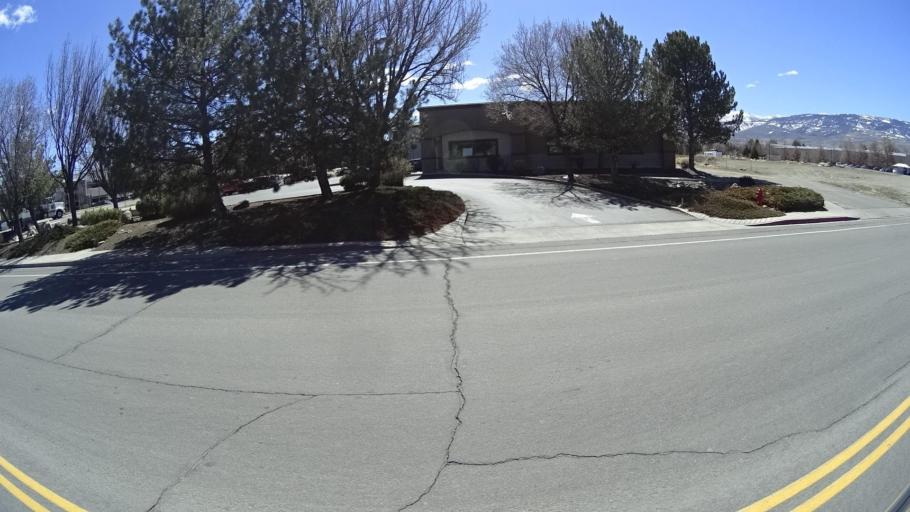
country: US
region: Nevada
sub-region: Washoe County
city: Sparks
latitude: 39.4616
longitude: -119.7736
